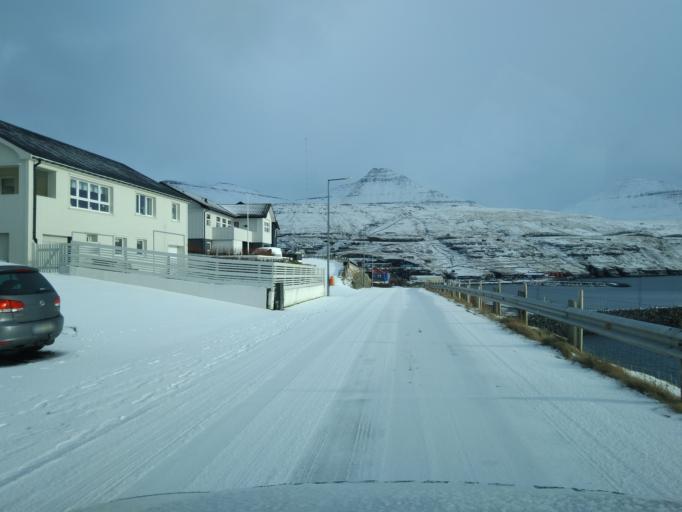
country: FO
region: Eysturoy
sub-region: Eidi
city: Eidi
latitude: 62.2988
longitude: -7.1008
